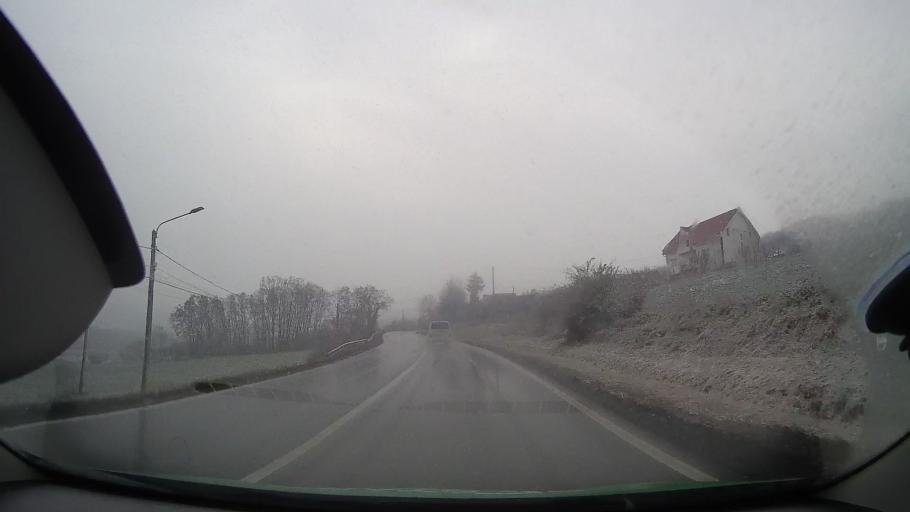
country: RO
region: Mures
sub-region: Comuna Bagaciu
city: Delenii
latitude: 46.2743
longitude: 24.3014
